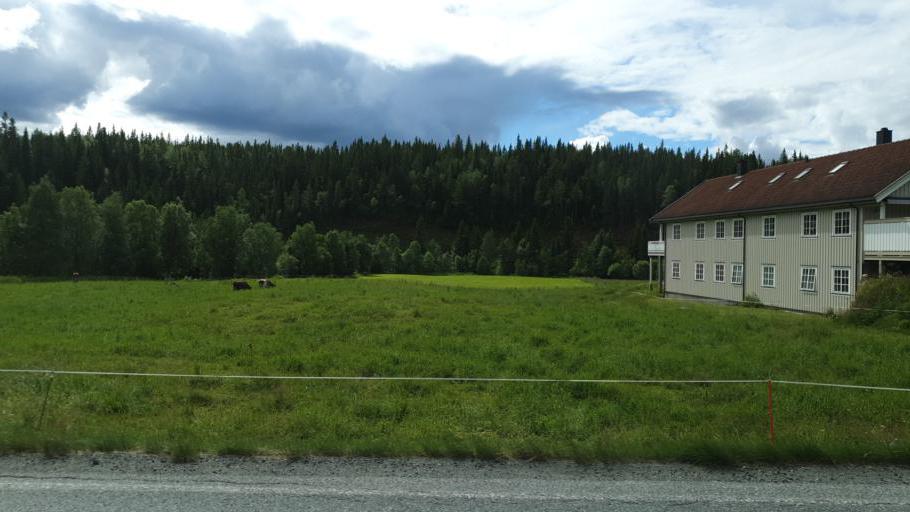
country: NO
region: Sor-Trondelag
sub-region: Rennebu
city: Berkak
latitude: 62.8669
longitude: 10.0674
